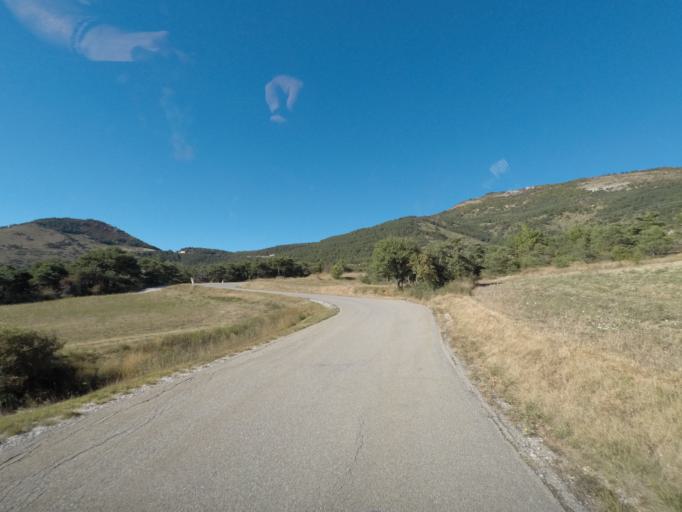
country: FR
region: Provence-Alpes-Cote d'Azur
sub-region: Departement des Hautes-Alpes
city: Serres
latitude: 44.4244
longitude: 5.5812
